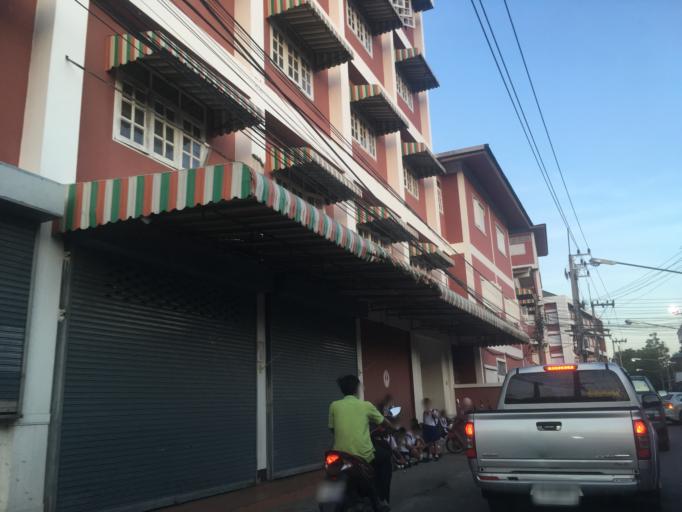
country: TH
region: Chon Buri
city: Ban Bueng
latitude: 13.3112
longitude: 101.1173
